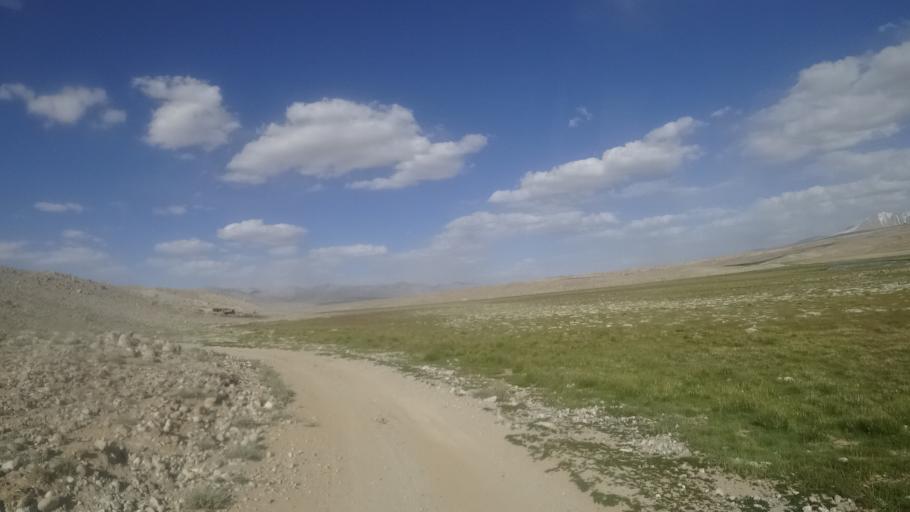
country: AF
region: Badakhshan
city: Khandud
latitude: 37.4154
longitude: 73.2279
